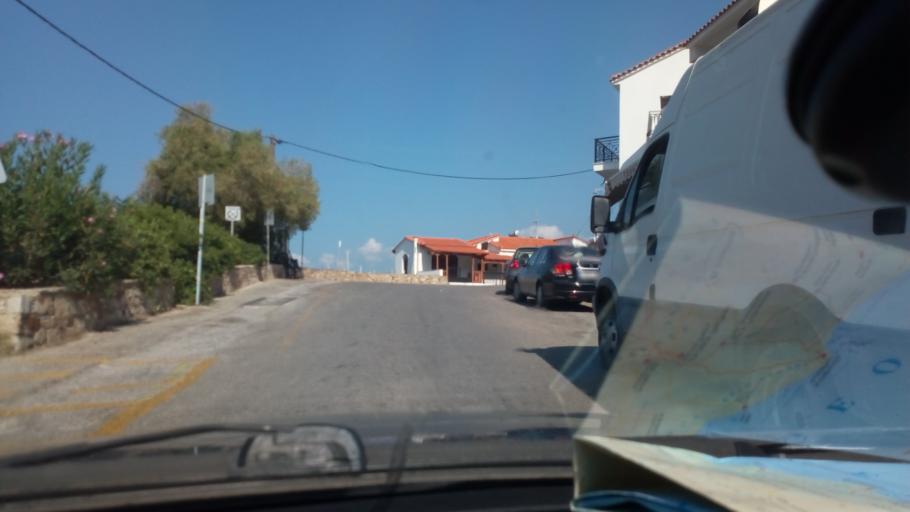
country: GR
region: North Aegean
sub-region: Nomos Samou
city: Agios Kirykos
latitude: 37.6329
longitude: 26.0885
